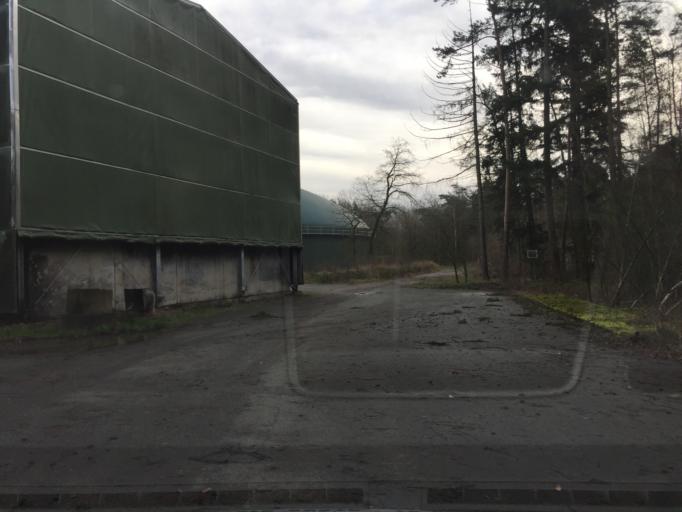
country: DE
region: Lower Saxony
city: Leese
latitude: 52.5229
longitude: 9.1355
